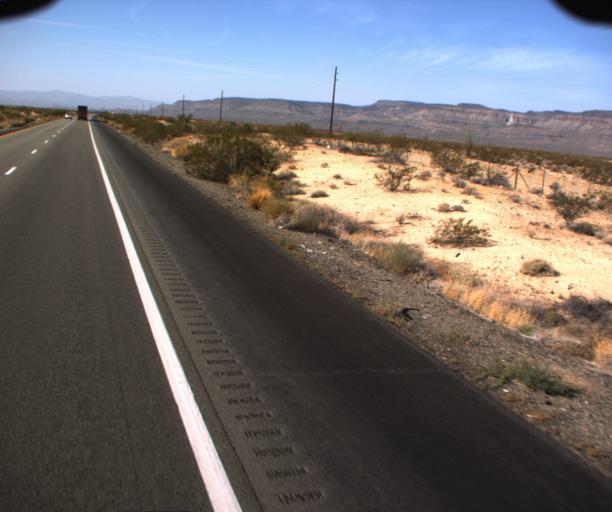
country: US
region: Arizona
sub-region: Mohave County
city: Kingman
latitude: 34.9424
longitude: -114.1476
